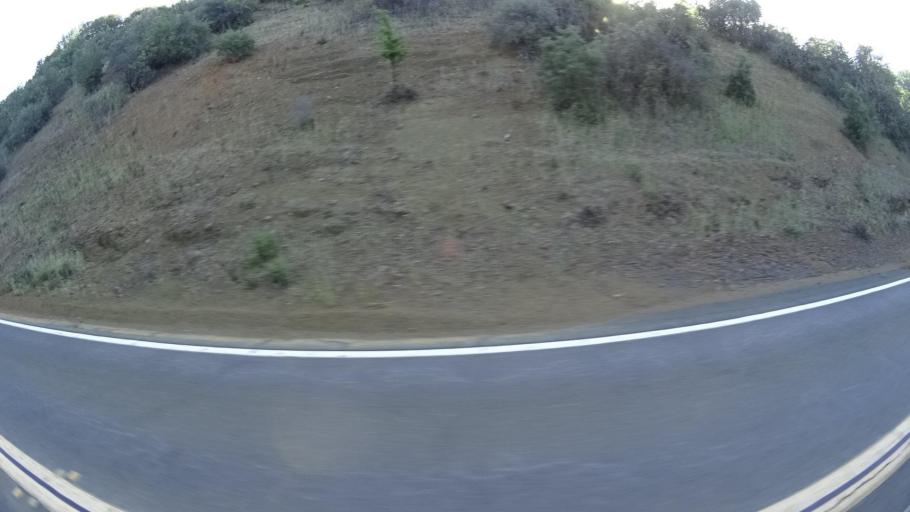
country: US
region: California
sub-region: Lake County
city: North Lakeport
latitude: 39.1031
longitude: -122.9694
